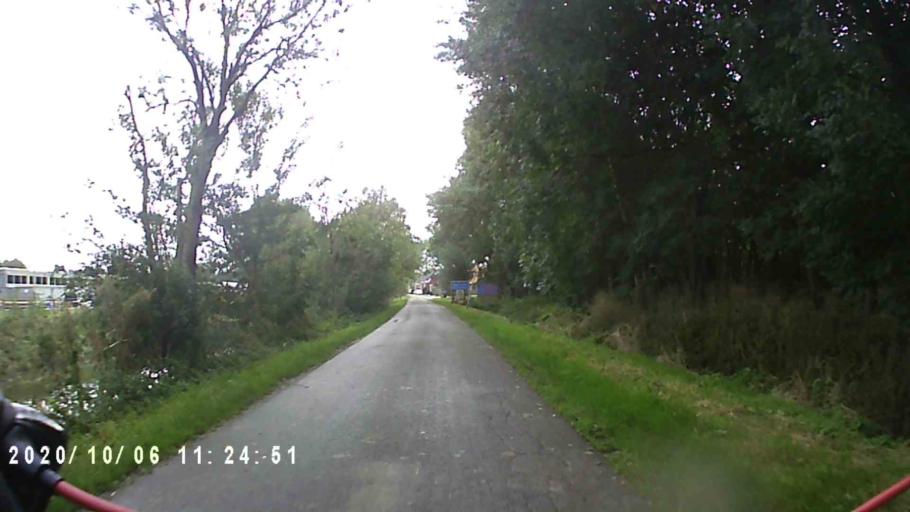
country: NL
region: Groningen
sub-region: Gemeente Zuidhorn
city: Oldehove
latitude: 53.3420
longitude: 6.4217
